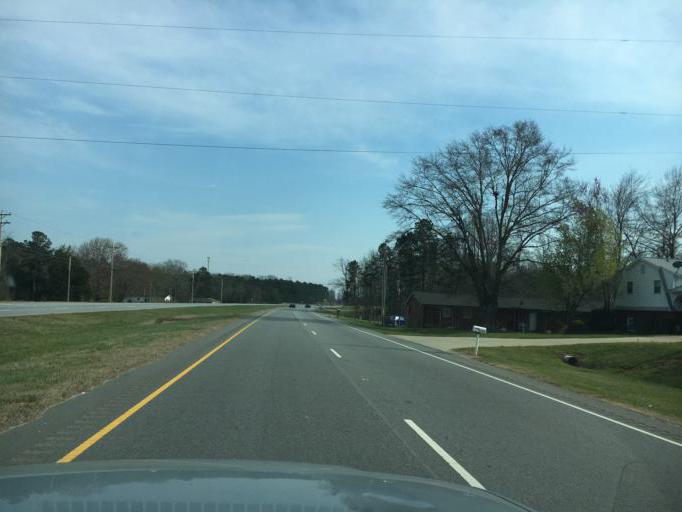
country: US
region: North Carolina
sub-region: Rutherford County
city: Forest City
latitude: 35.2813
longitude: -81.8987
